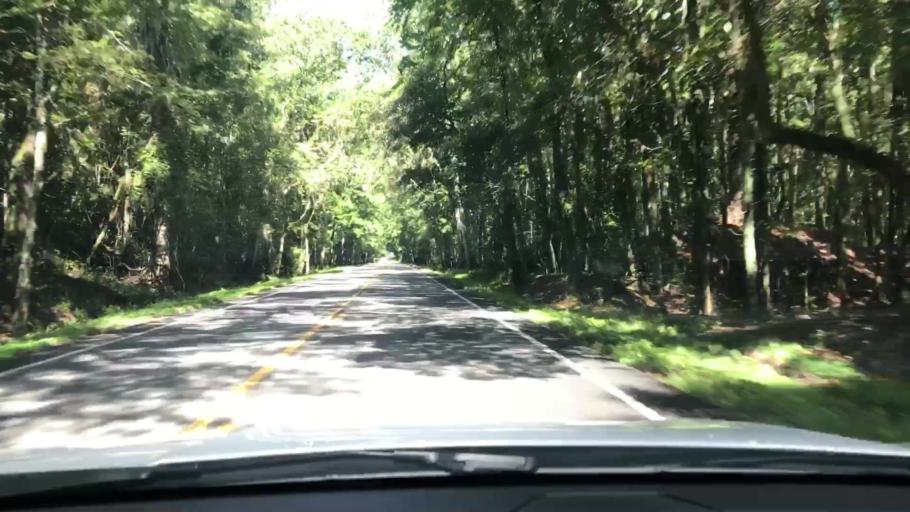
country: US
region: South Carolina
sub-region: Berkeley County
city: Hanahan
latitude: 32.8820
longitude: -80.1040
